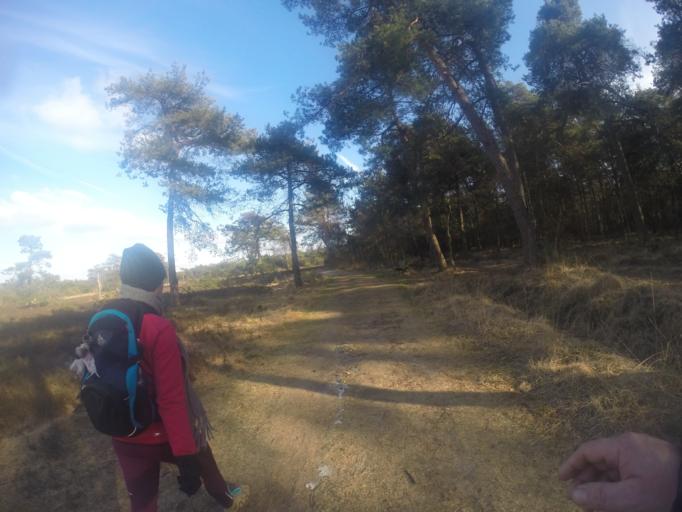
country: NL
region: Gelderland
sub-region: Gemeente Lochem
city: Almen
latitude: 52.1333
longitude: 6.3420
